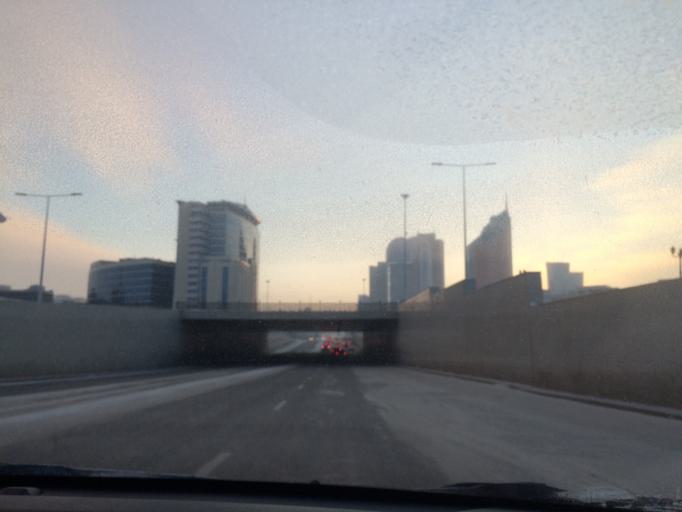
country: KZ
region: Astana Qalasy
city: Astana
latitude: 51.1340
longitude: 71.4089
